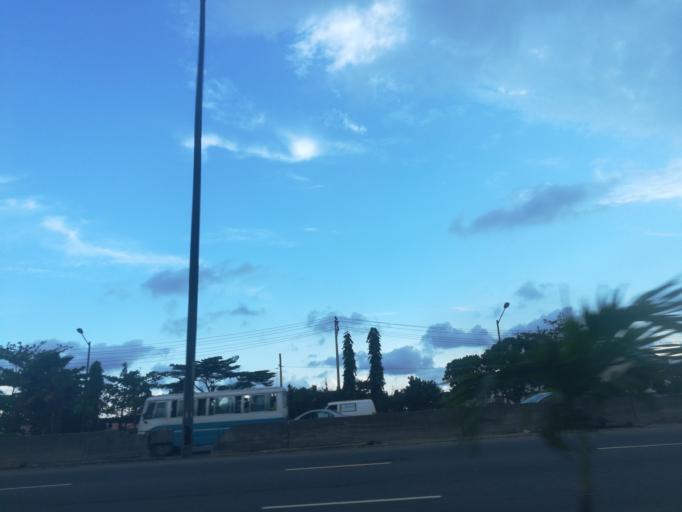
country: NG
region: Lagos
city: Somolu
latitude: 6.5482
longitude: 3.3808
